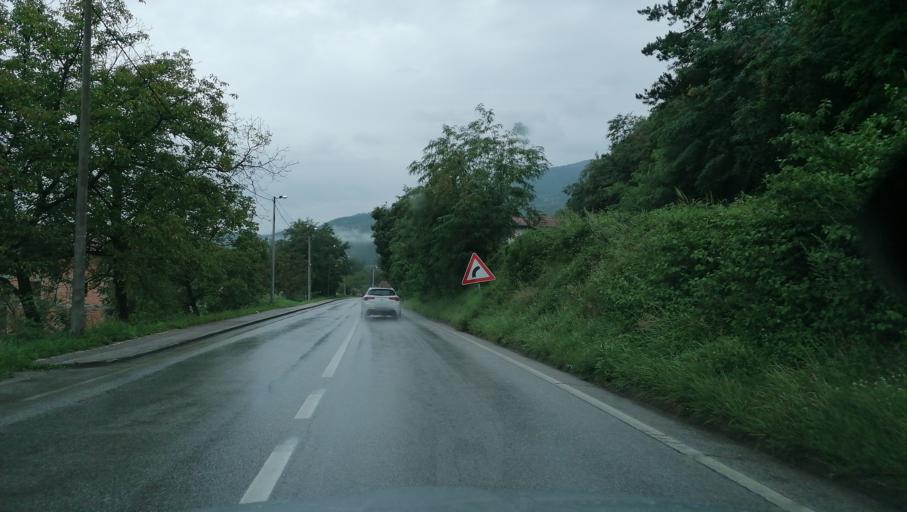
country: BA
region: Federation of Bosnia and Herzegovina
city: Gorazde
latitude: 43.6812
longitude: 19.0125
